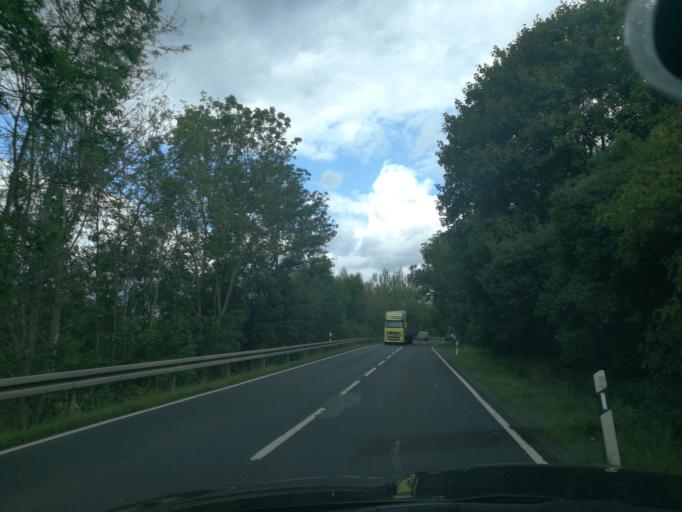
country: DE
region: Saxony
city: Oelsnitz
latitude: 50.3967
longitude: 12.1879
